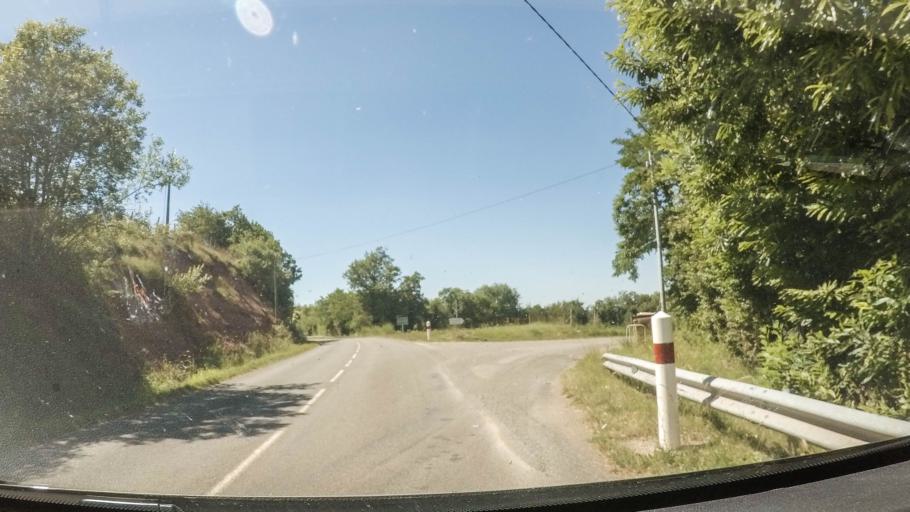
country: FR
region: Midi-Pyrenees
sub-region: Departement de l'Aveyron
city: Saint-Christophe-Vallon
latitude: 44.4736
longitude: 2.3564
